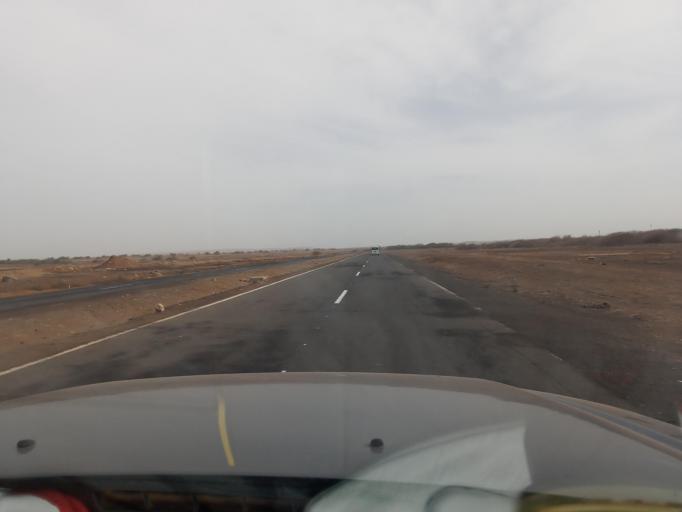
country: CV
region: Sal
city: Espargos
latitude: 16.6869
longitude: -22.9374
